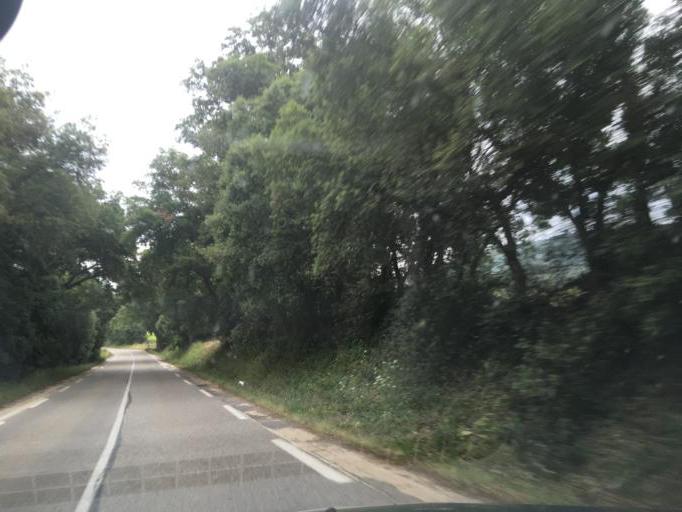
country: FR
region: Provence-Alpes-Cote d'Azur
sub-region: Departement du Var
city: Pierrefeu-du-Var
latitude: 43.2330
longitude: 6.1971
